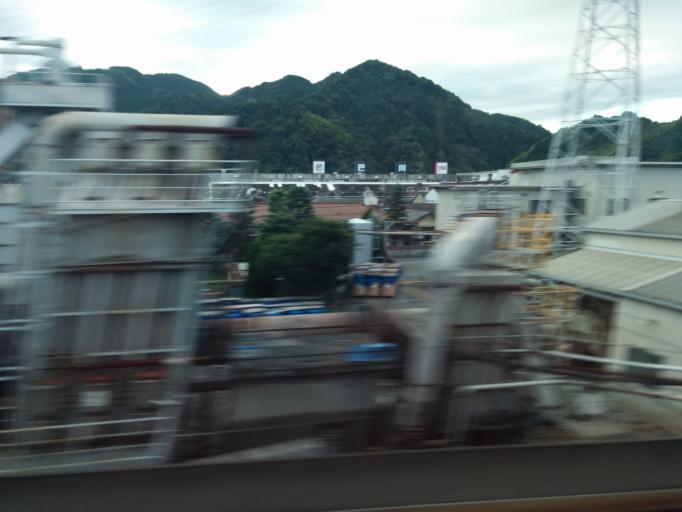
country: JP
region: Shizuoka
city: Shizuoka-shi
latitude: 34.9299
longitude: 138.3626
